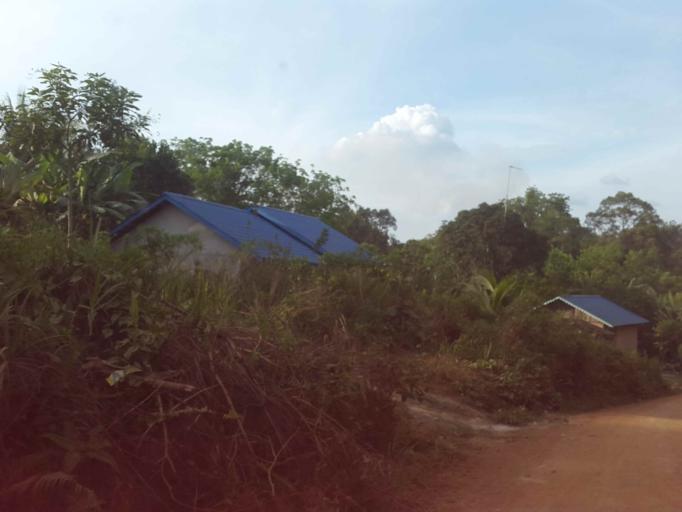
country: MY
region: Sarawak
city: Simanggang
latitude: 0.5448
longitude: 111.4251
